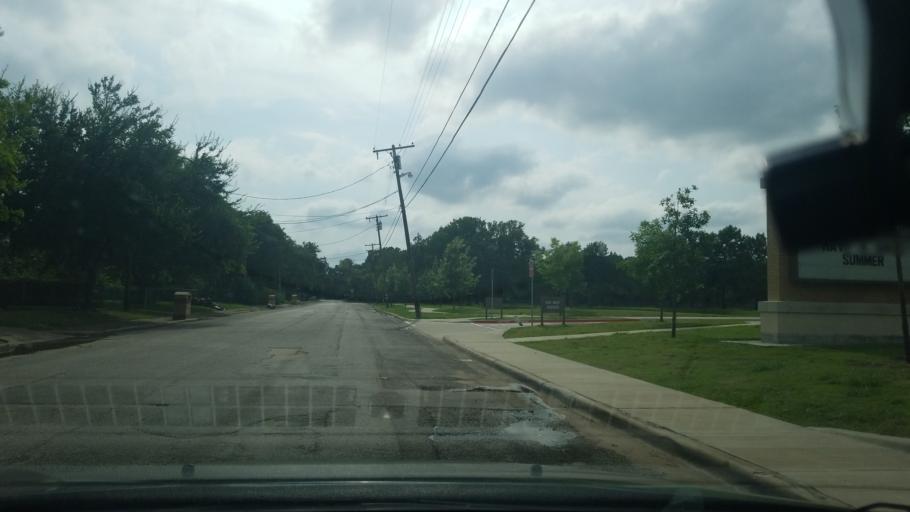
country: US
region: Texas
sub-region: Dallas County
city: Balch Springs
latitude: 32.7576
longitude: -96.6340
